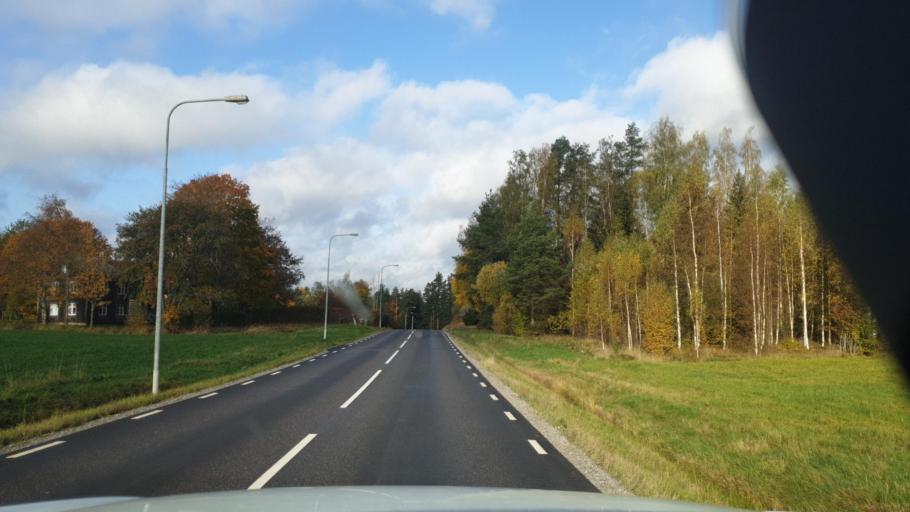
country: SE
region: Vaermland
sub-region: Arvika Kommun
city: Arvika
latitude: 59.5425
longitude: 12.5799
